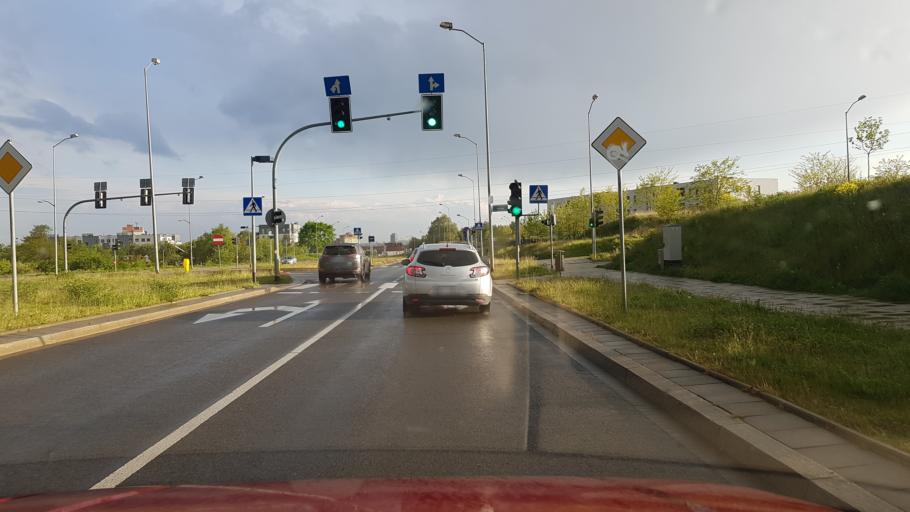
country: PL
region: West Pomeranian Voivodeship
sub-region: Szczecin
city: Szczecin
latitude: 53.4599
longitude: 14.5525
